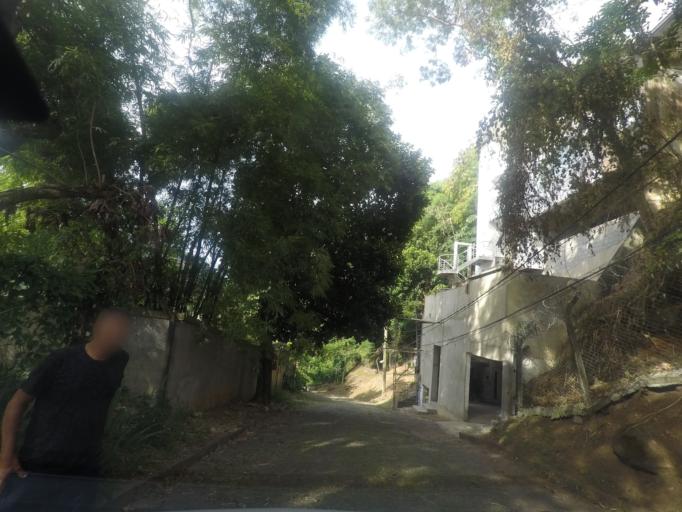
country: BR
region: Rio de Janeiro
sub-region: Rio De Janeiro
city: Rio de Janeiro
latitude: -22.9617
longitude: -43.1997
